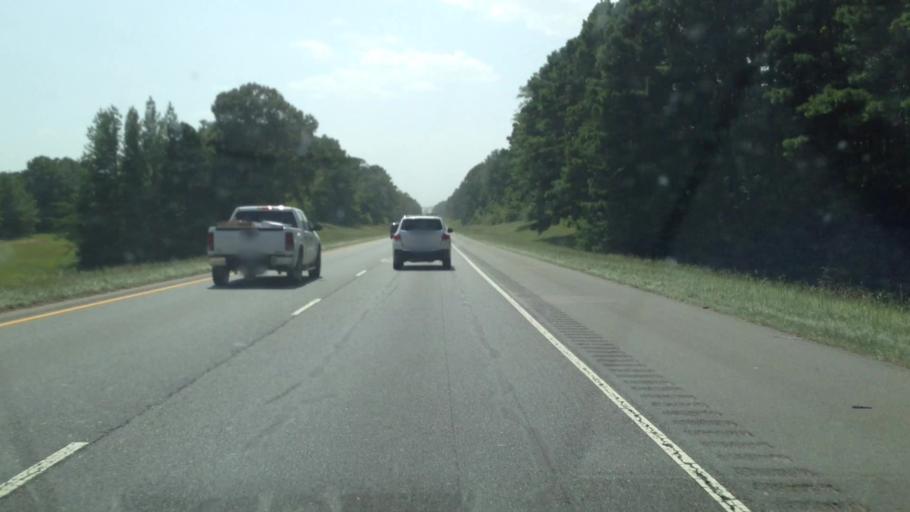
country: US
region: Louisiana
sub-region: Bossier Parish
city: Eastwood
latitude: 32.5423
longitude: -93.5531
